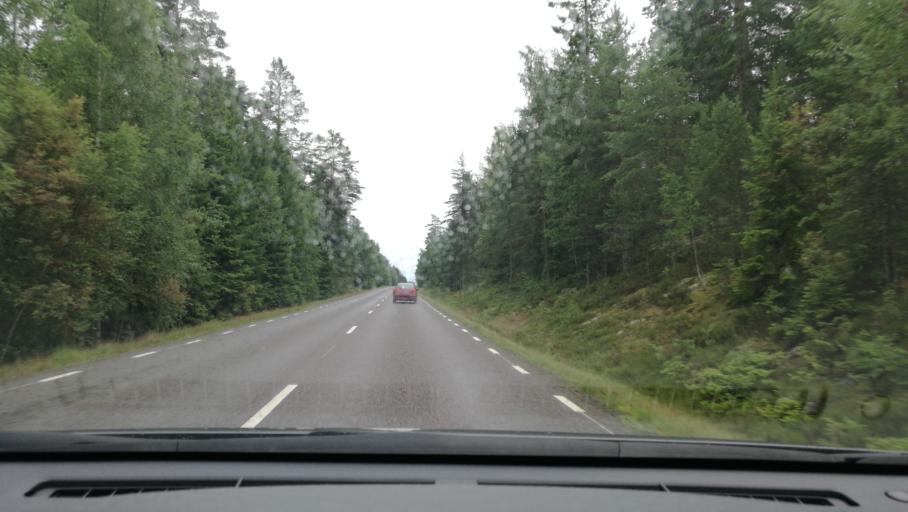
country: SE
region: OEstergoetland
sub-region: Norrkopings Kommun
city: Svartinge
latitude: 58.7692
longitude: 15.9699
